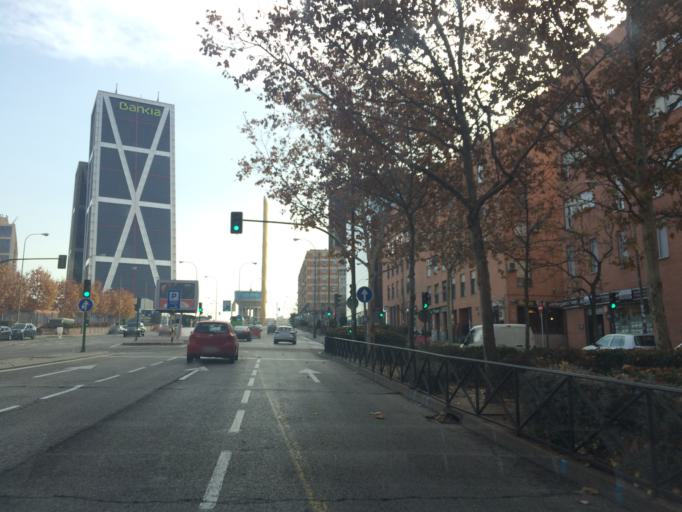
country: ES
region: Madrid
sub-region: Provincia de Madrid
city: Chamartin
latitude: 40.4680
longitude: -3.6935
